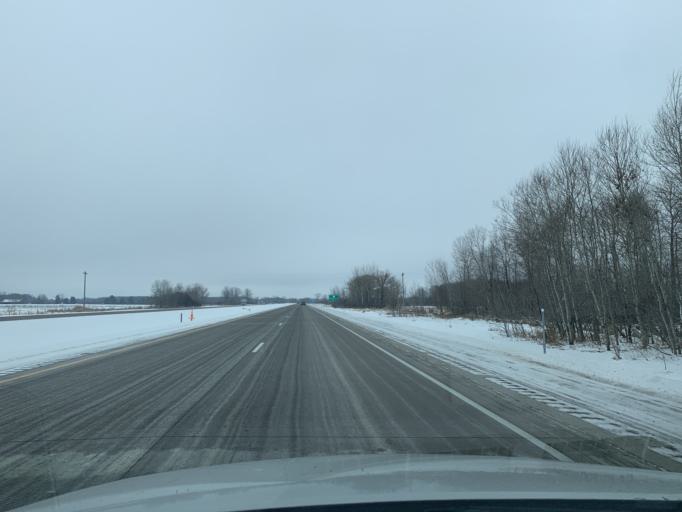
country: US
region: Minnesota
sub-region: Chisago County
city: Rush City
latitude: 45.7036
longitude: -92.9925
